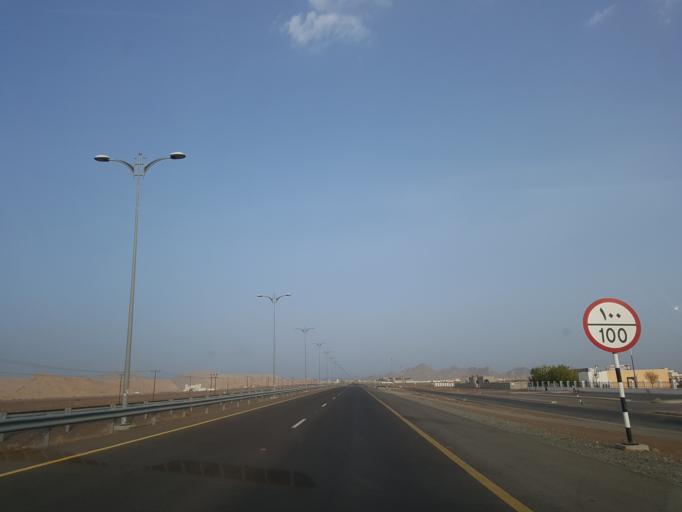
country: OM
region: Al Buraimi
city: Al Buraymi
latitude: 24.2358
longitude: 55.9161
